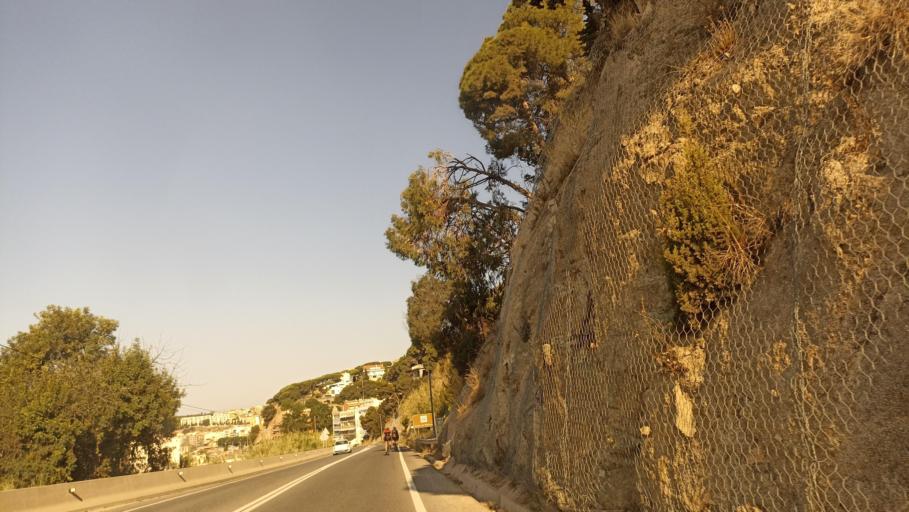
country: ES
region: Catalonia
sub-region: Provincia de Barcelona
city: Arenys de Mar
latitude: 41.5807
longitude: 2.5631
